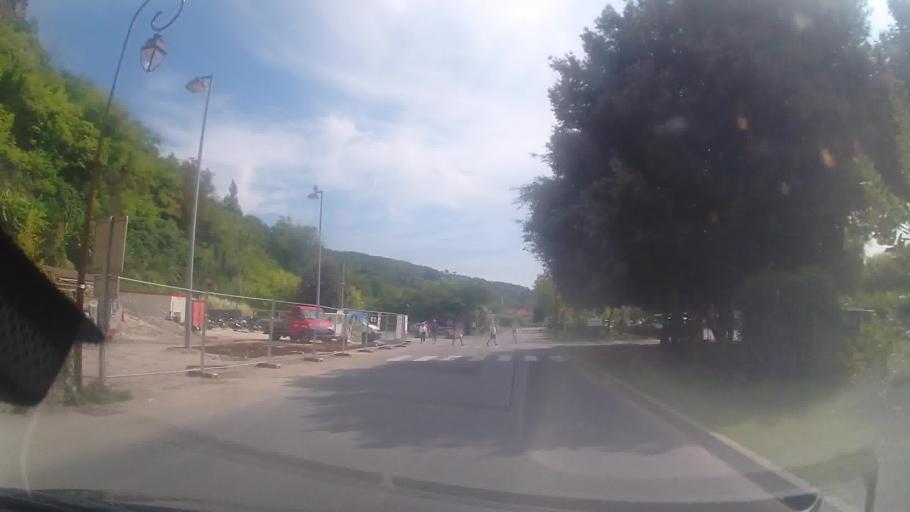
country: FR
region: Aquitaine
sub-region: Departement de la Dordogne
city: Cenac-et-Saint-Julien
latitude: 44.8258
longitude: 1.1836
